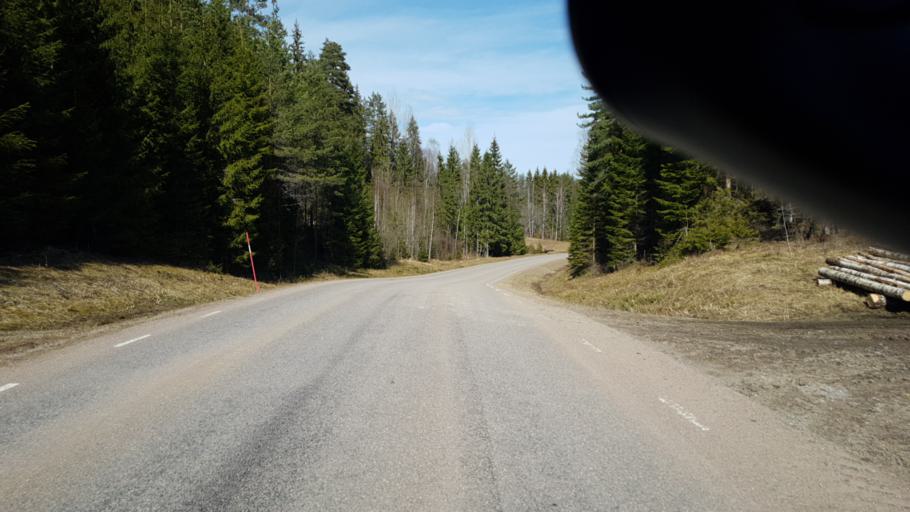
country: SE
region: Vaermland
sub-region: Arvika Kommun
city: Arvika
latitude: 59.6133
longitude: 12.7825
